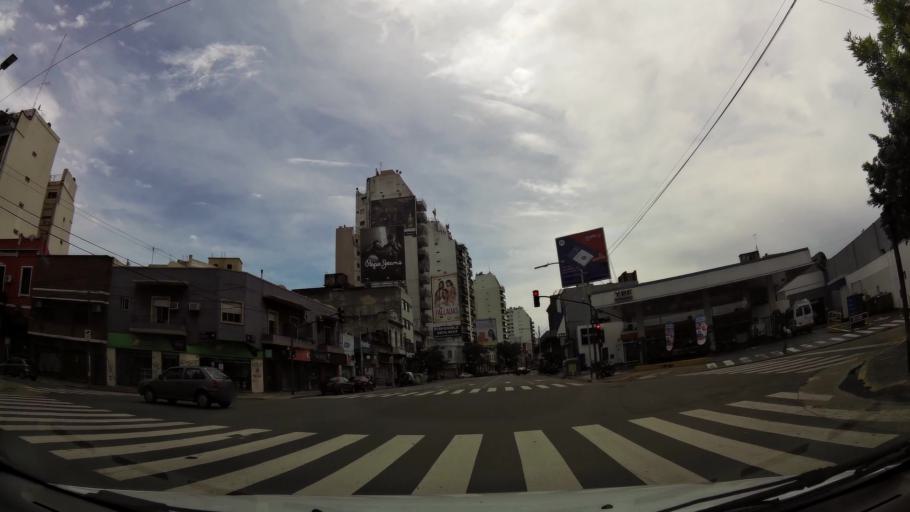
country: AR
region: Buenos Aires F.D.
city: Colegiales
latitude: -34.5964
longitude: -58.4260
